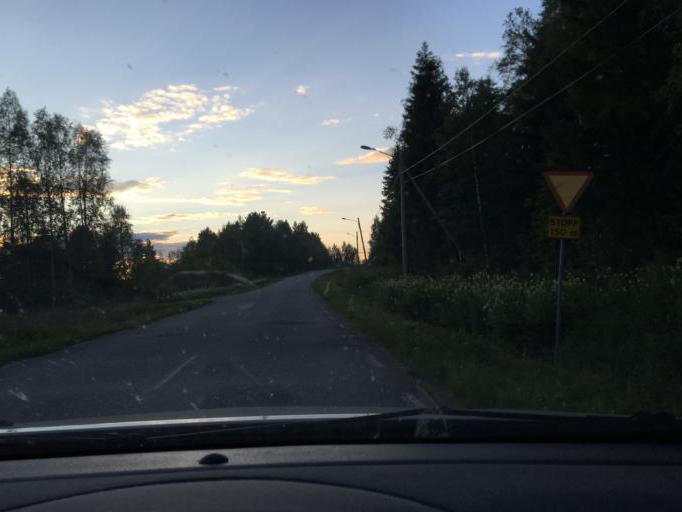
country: SE
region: Norrbotten
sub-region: Kalix Kommun
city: Rolfs
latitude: 65.9033
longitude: 22.9309
